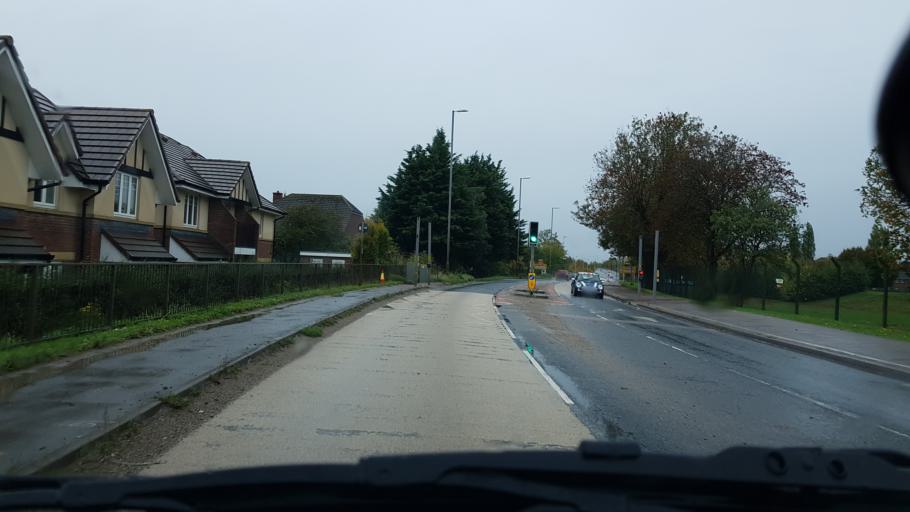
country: GB
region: England
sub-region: Worcestershire
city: Bredon
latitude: 51.9980
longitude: -2.1000
